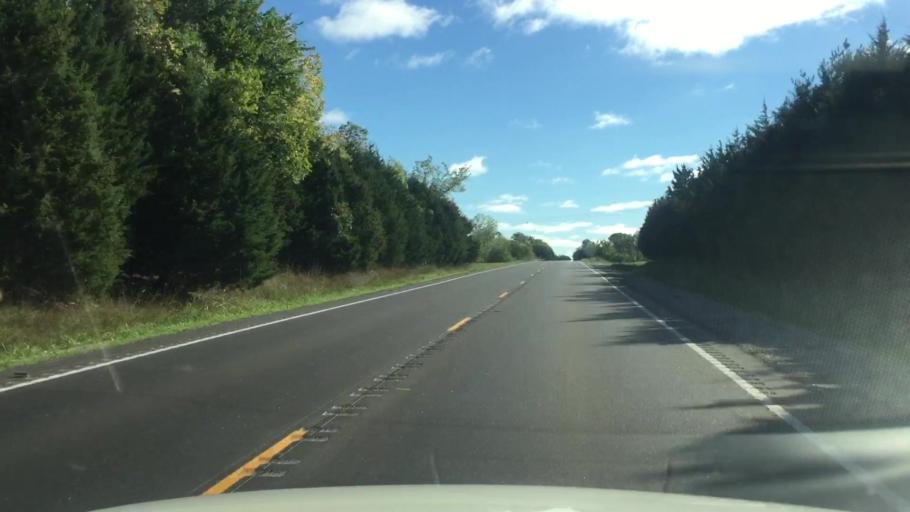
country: US
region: Missouri
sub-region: Boone County
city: Columbia
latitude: 38.9899
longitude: -92.5214
